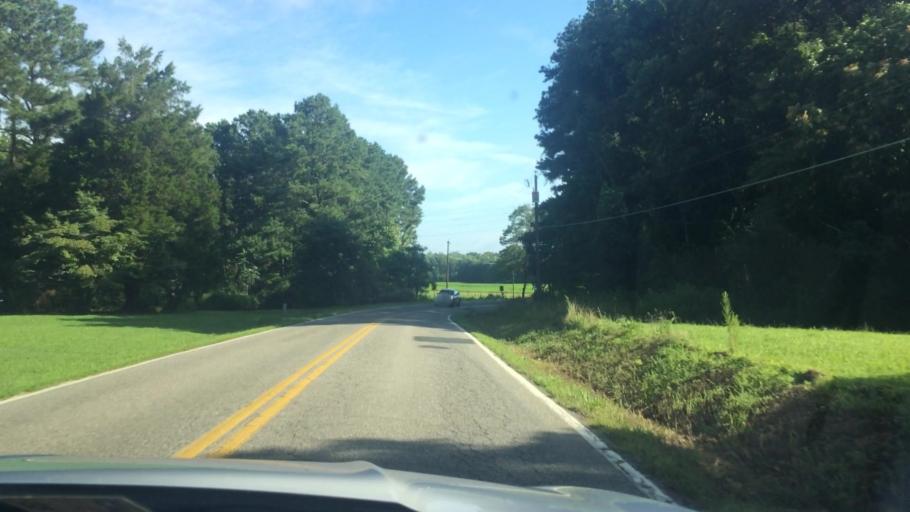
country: US
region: Virginia
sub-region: Middlesex County
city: Deltaville
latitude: 37.5806
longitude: -76.4566
